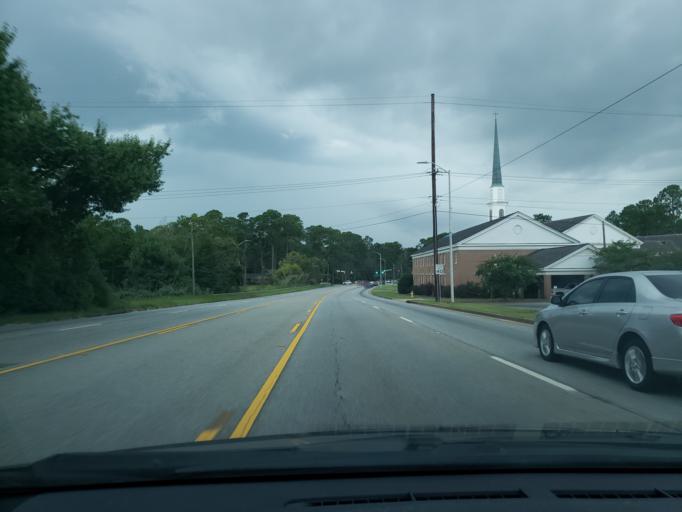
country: US
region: Georgia
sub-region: Dougherty County
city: Albany
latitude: 31.5900
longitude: -84.1895
